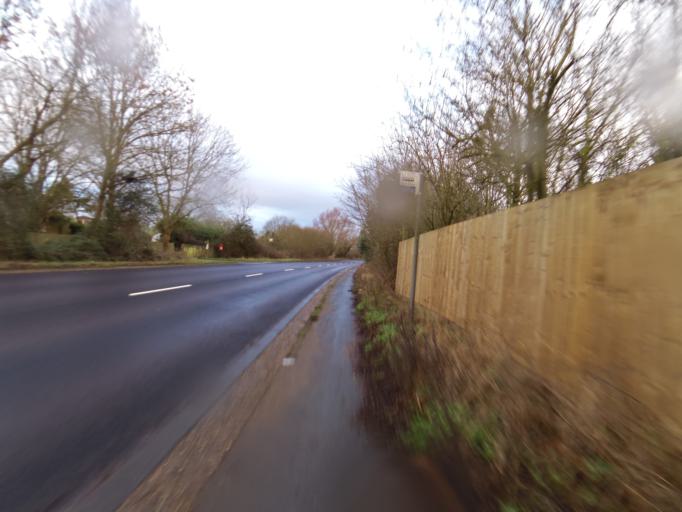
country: GB
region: England
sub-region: Suffolk
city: Needham Market
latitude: 52.1674
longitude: 1.0299
